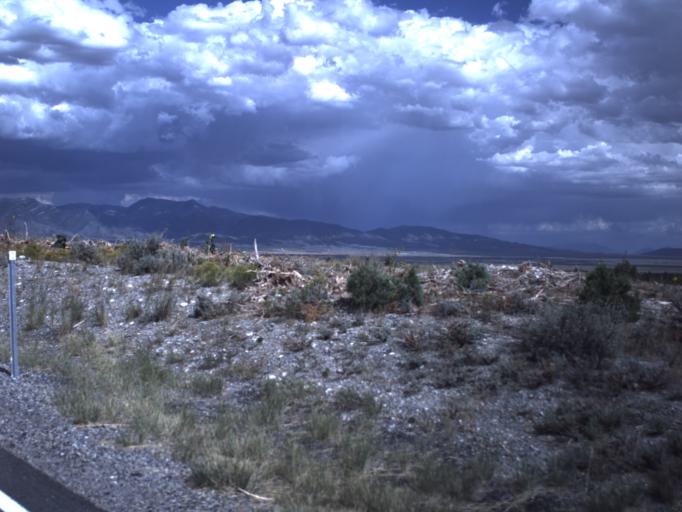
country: US
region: Utah
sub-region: Tooele County
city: Grantsville
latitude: 40.3333
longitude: -112.5104
